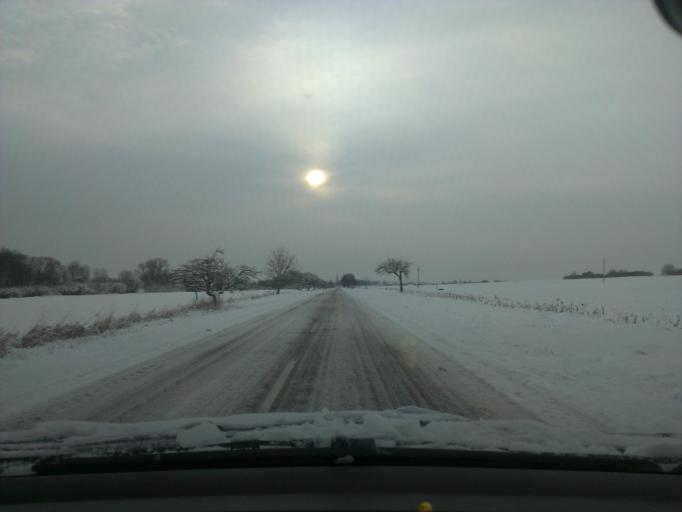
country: SK
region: Trnavsky
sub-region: Okres Trnava
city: Piestany
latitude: 48.5385
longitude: 17.9488
